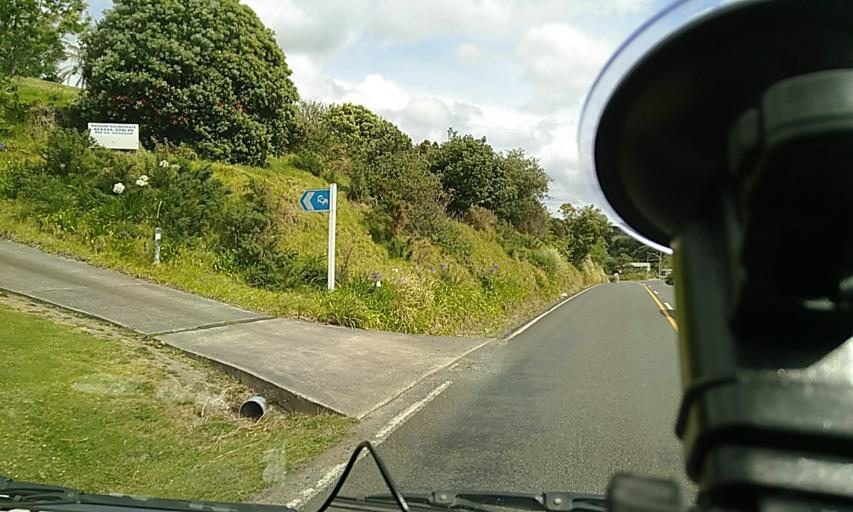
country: NZ
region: Northland
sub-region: Far North District
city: Ahipara
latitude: -35.5143
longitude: 173.3890
